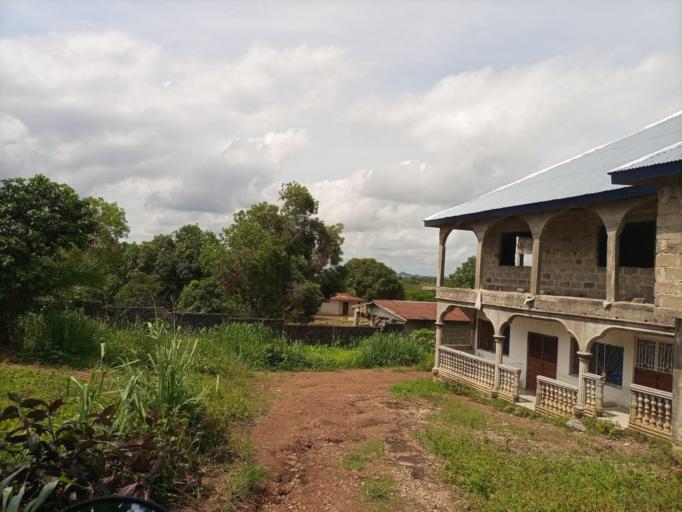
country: SL
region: Southern Province
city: Bo
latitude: 7.9740
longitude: -11.7605
